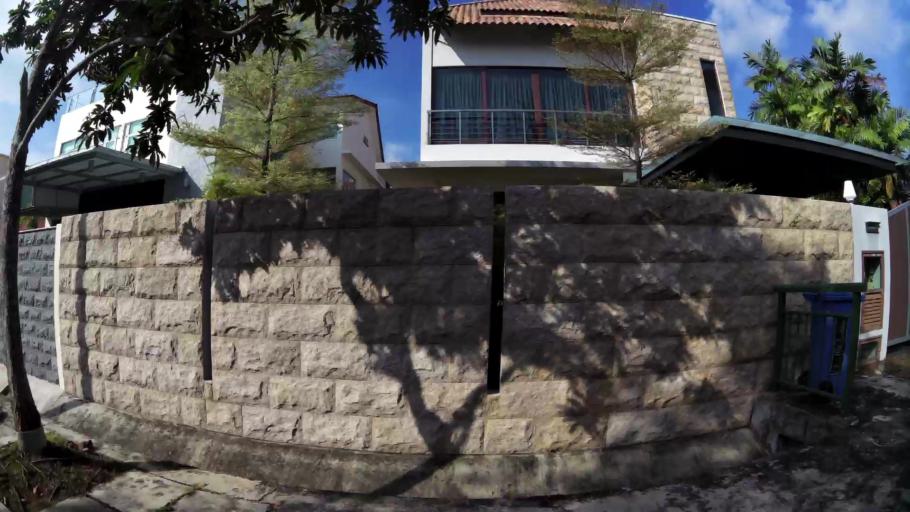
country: SG
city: Singapore
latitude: 1.3130
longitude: 103.9206
